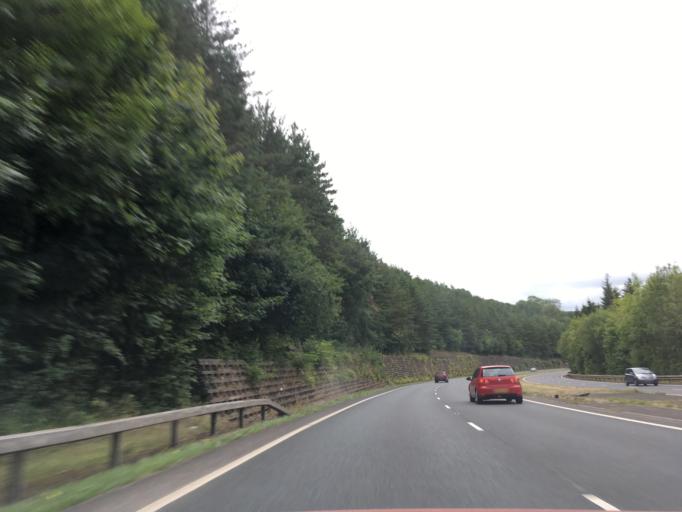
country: GB
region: Wales
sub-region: Sir Powys
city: Brecon
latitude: 51.9363
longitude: -3.3774
